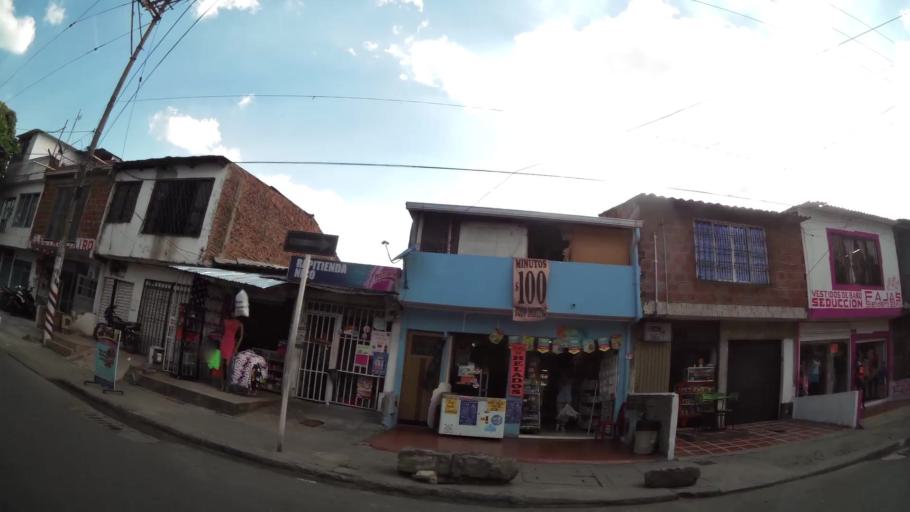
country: CO
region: Valle del Cauca
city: Cali
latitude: 3.4175
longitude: -76.4958
